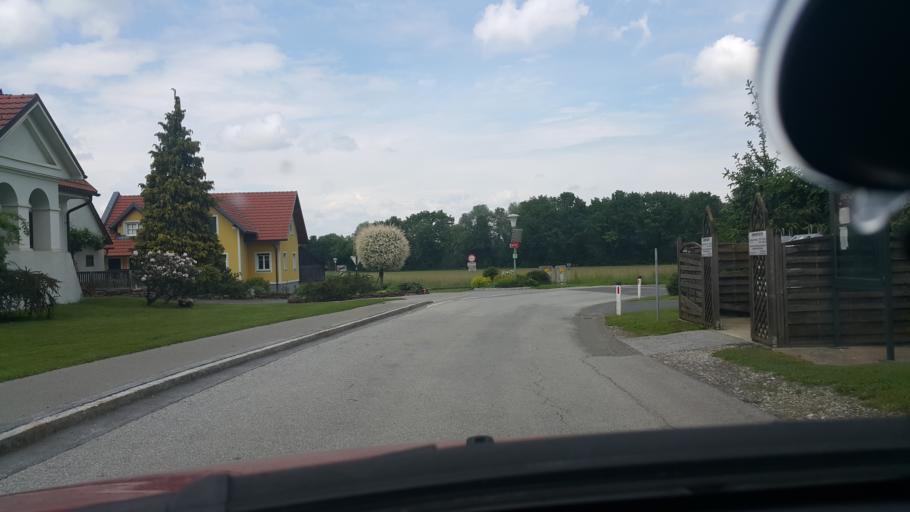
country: AT
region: Styria
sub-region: Politischer Bezirk Leibnitz
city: Weitendorf
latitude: 46.8807
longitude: 15.4807
